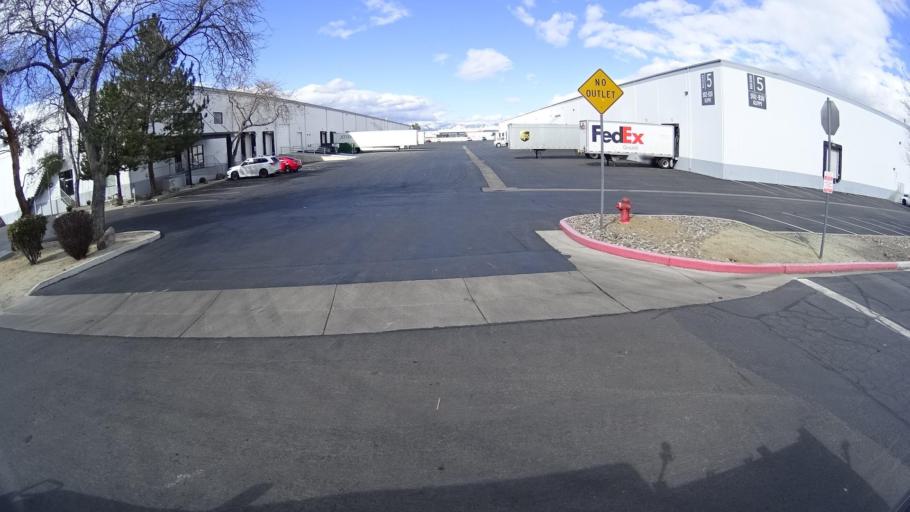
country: US
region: Nevada
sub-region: Washoe County
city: Sparks
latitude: 39.5232
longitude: -119.7263
